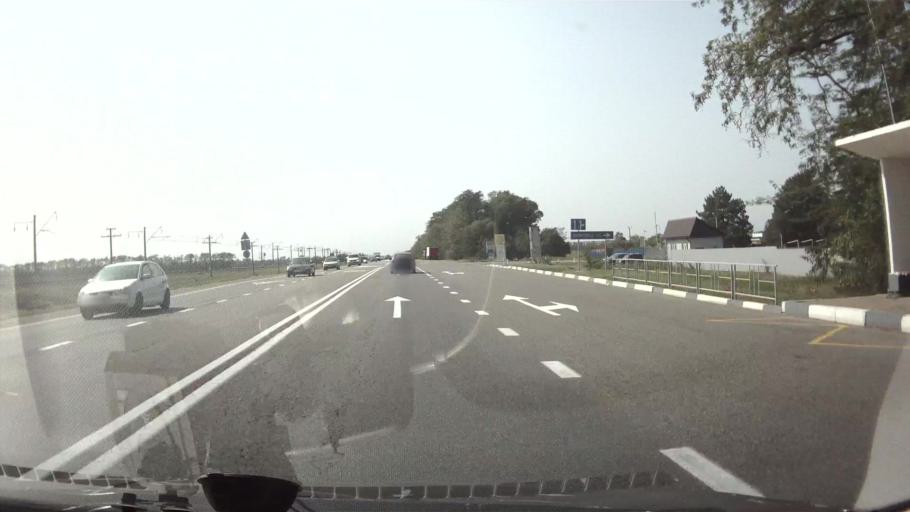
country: RU
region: Krasnodarskiy
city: Ladozhskaya
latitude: 45.3014
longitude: 39.8941
